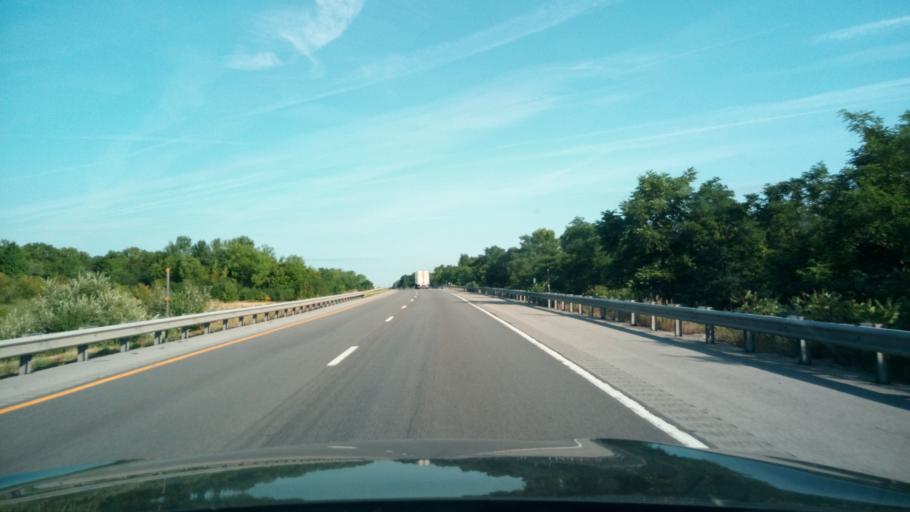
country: US
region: New York
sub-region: Livingston County
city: Mount Morris
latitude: 42.6418
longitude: -77.7889
